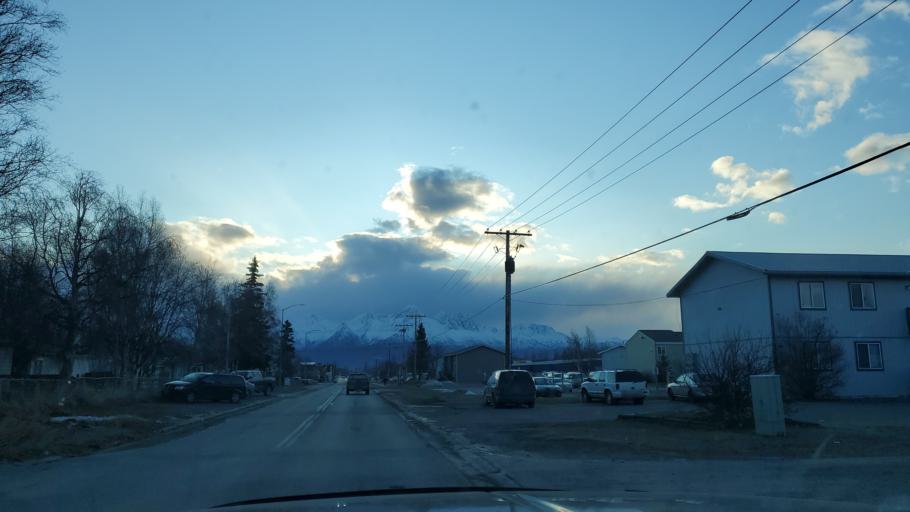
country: US
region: Alaska
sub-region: Matanuska-Susitna Borough
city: Palmer
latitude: 61.6044
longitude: -149.1184
